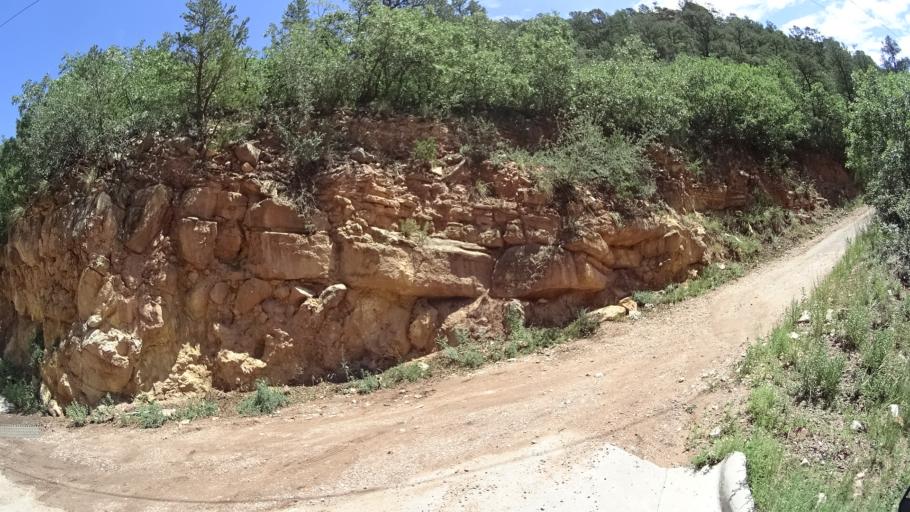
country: US
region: Colorado
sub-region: El Paso County
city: Manitou Springs
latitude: 38.8653
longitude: -104.9176
